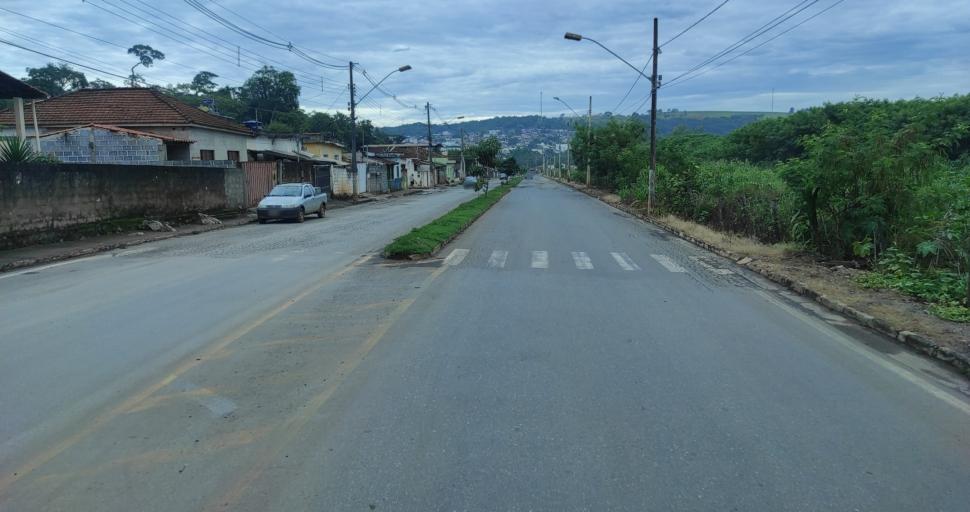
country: BR
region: Minas Gerais
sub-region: Arcos
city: Arcos
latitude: -20.3772
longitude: -45.6687
